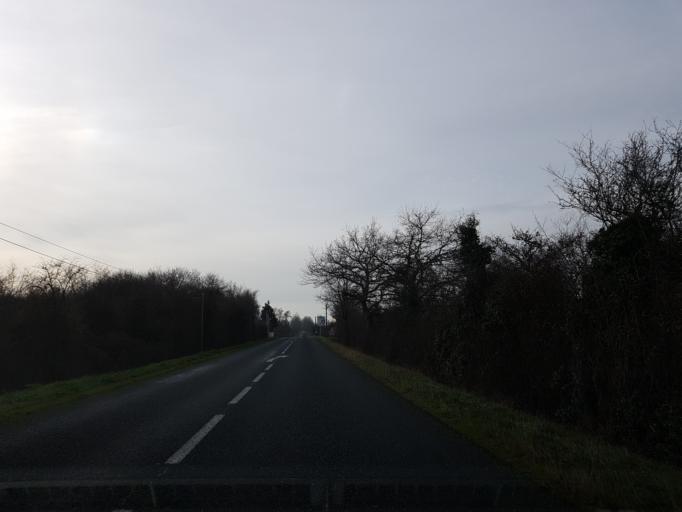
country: FR
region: Auvergne
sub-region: Departement de l'Allier
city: Lusigny
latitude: 46.6137
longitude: 3.5587
